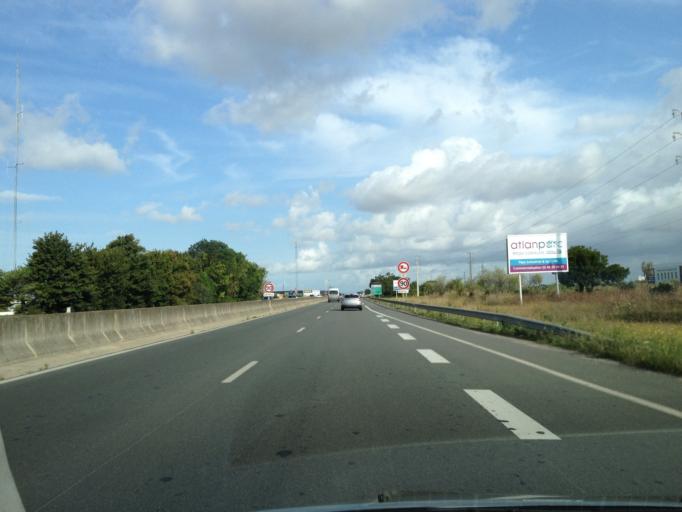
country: FR
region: Poitou-Charentes
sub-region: Departement de la Charente-Maritime
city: Perigny
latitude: 46.1572
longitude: -1.1177
